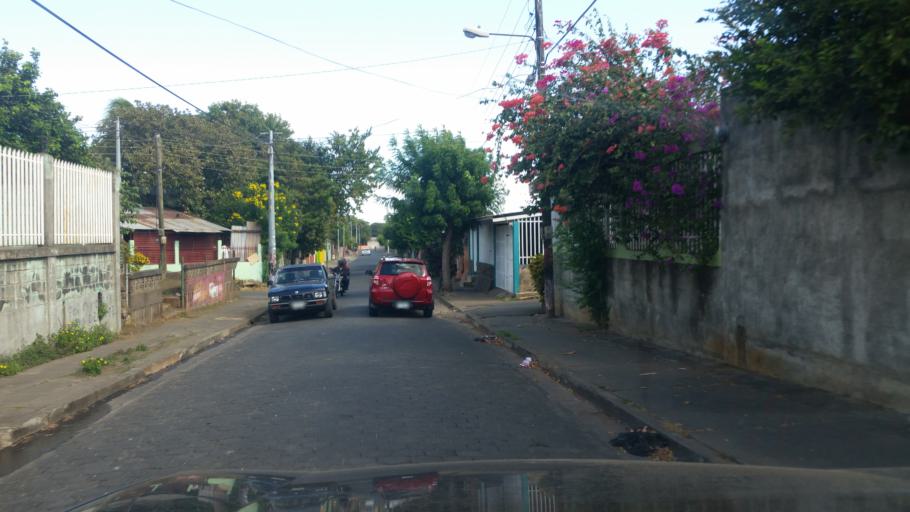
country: NI
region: Managua
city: Managua
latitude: 12.1297
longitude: -86.2364
